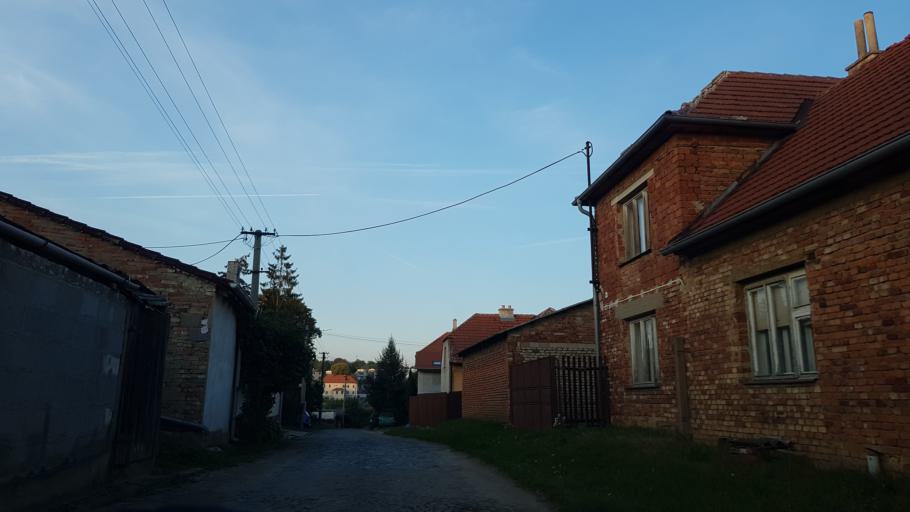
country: CZ
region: Zlin
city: Polesovice
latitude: 49.0311
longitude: 17.3392
